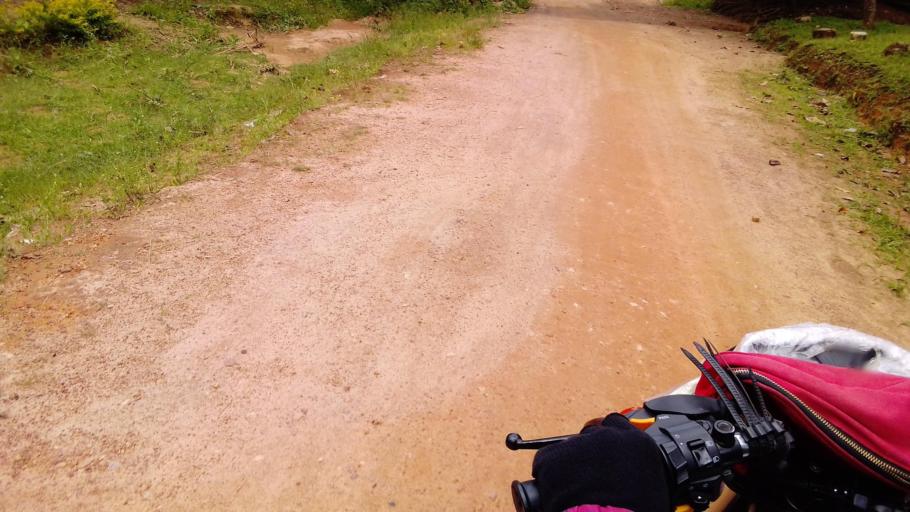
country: SL
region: Eastern Province
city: Koyima
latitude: 8.6963
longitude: -11.0107
